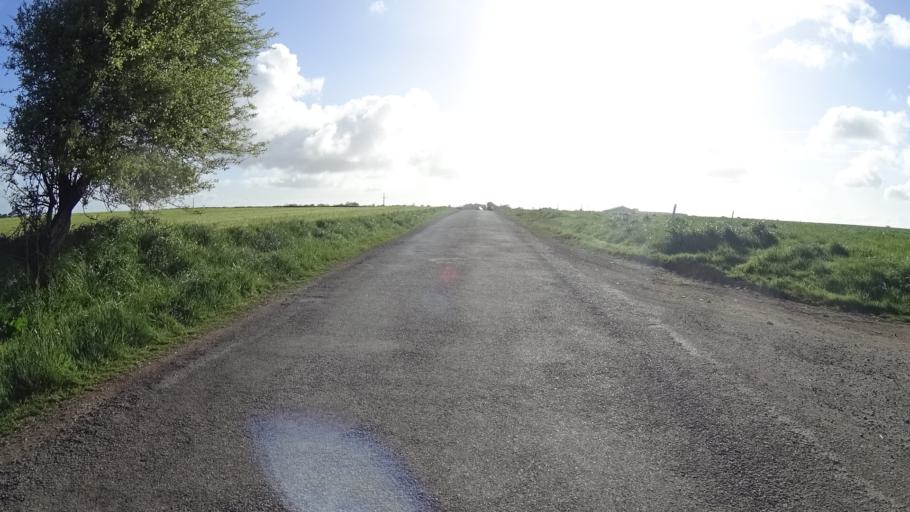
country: FR
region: Brittany
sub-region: Departement du Finistere
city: Ploumoguer
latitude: 48.4209
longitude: -4.6945
